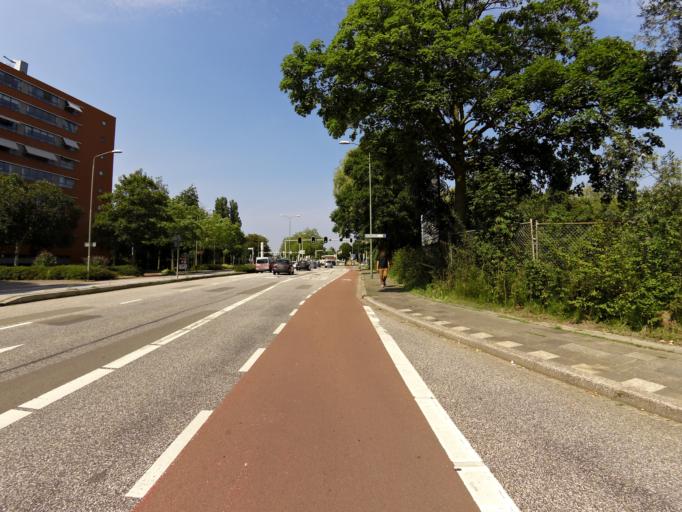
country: NL
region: South Holland
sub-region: Gemeente Dordrecht
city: Dordrecht
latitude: 51.7959
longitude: 4.6680
